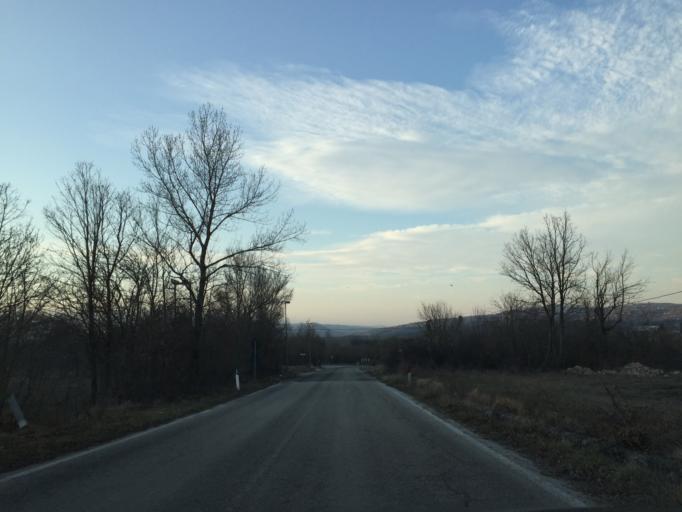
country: IT
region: Molise
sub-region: Provincia di Campobasso
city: Guardiaregia
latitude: 41.4543
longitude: 14.5563
